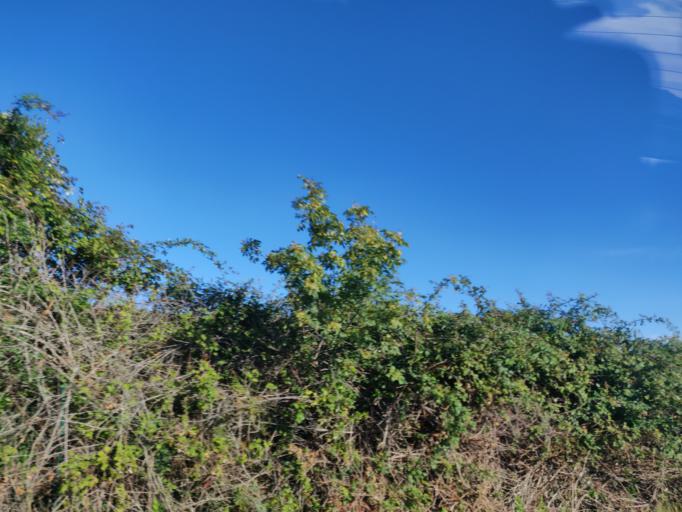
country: IT
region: Tuscany
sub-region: Provincia di Grosseto
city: Follonica
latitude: 42.9521
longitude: 10.7788
